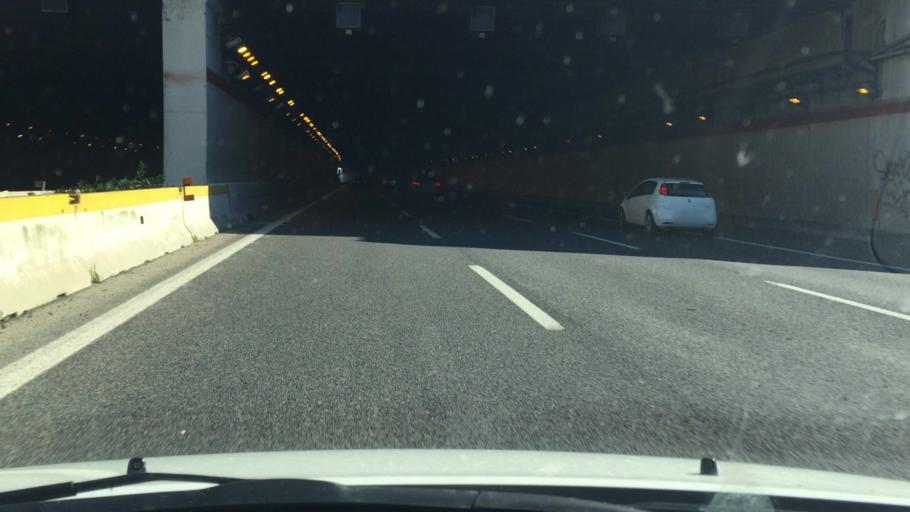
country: VA
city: Vatican City
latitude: 41.9816
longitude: 12.4500
